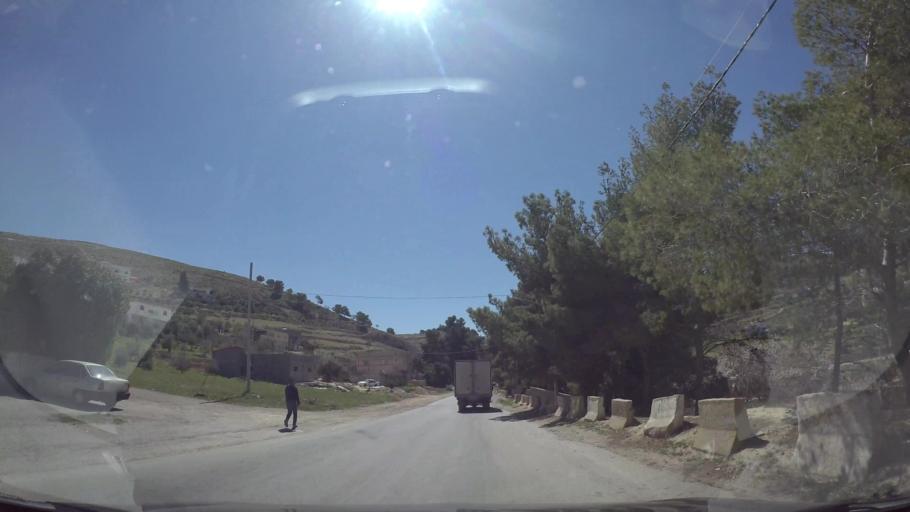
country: JO
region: Tafielah
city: At Tafilah
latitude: 30.8198
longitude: 35.5867
